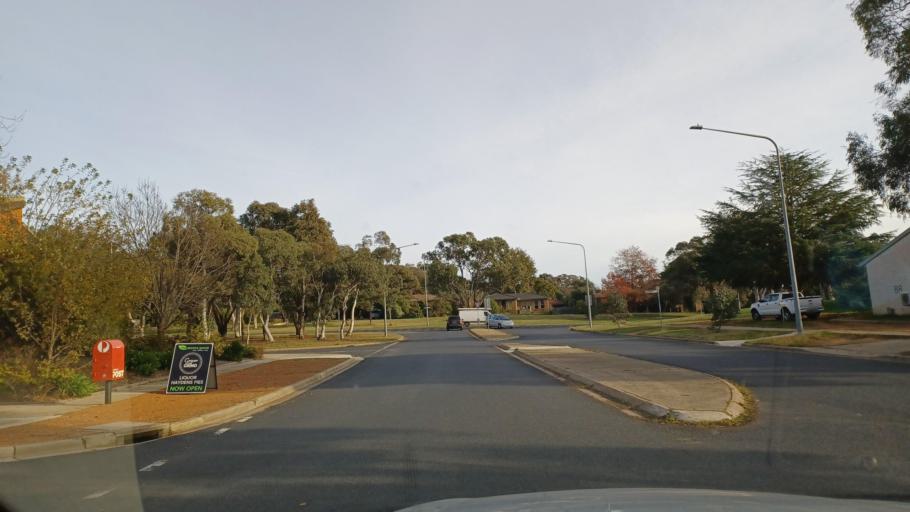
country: AU
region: Australian Capital Territory
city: Belconnen
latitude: -35.1944
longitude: 149.0621
